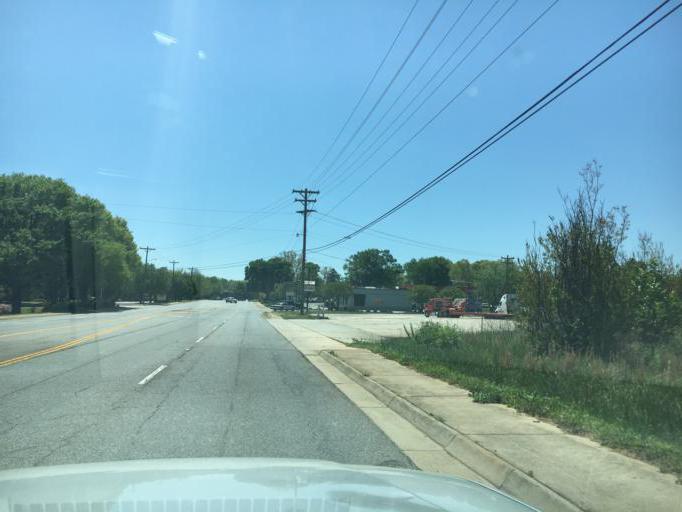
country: US
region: South Carolina
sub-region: Greenville County
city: Greer
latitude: 34.9165
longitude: -82.2375
